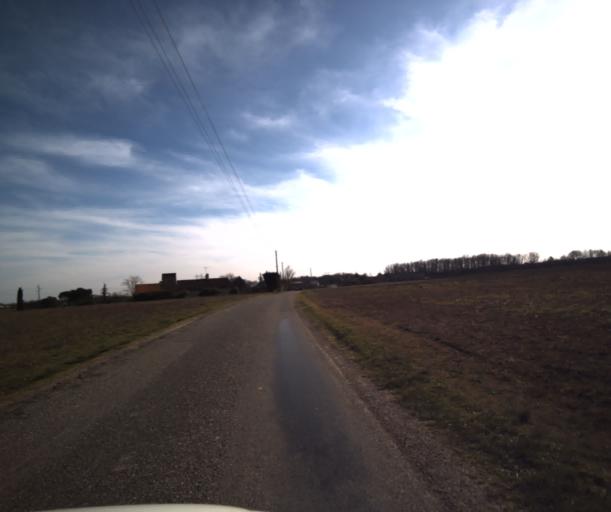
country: FR
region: Midi-Pyrenees
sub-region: Departement du Tarn-et-Garonne
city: Campsas
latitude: 43.9244
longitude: 1.3270
